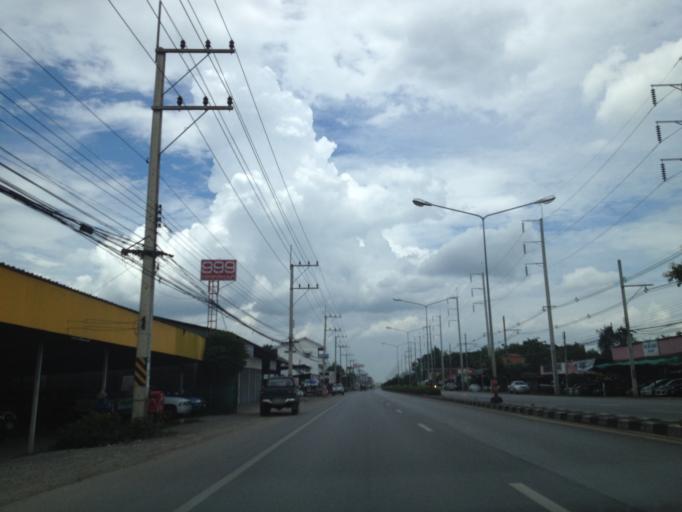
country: TH
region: Chiang Mai
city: San Pa Tong
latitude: 18.6382
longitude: 98.8995
